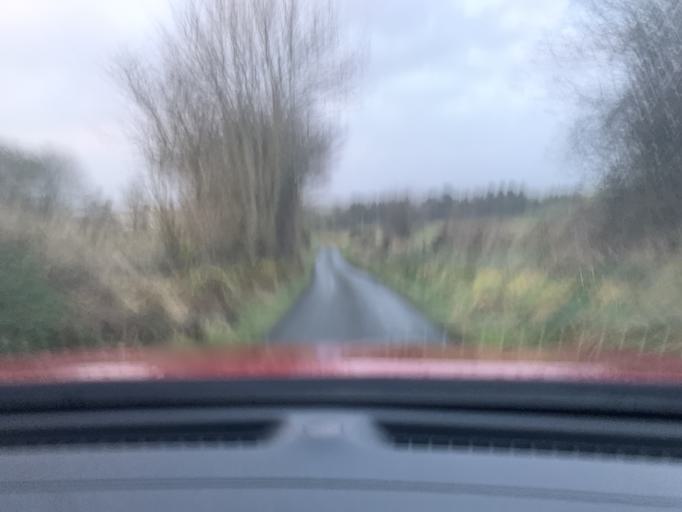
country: IE
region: Connaught
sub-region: Sligo
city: Ballymote
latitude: 54.0705
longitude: -8.3939
